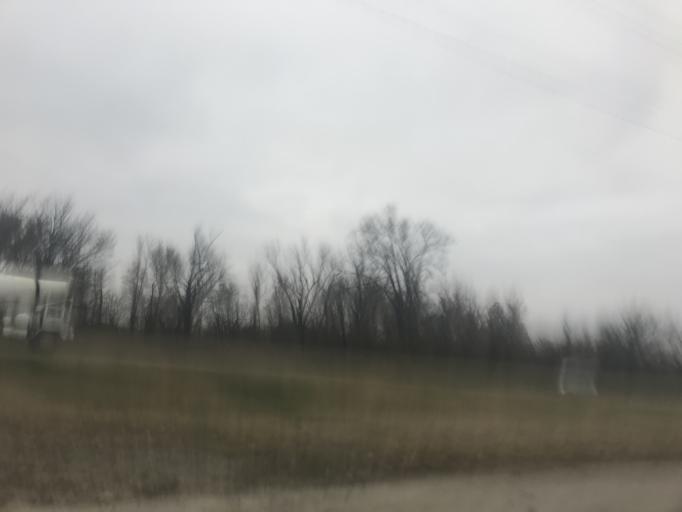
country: US
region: Indiana
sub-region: Clark County
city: Jeffersonville
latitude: 38.2678
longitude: -85.7175
